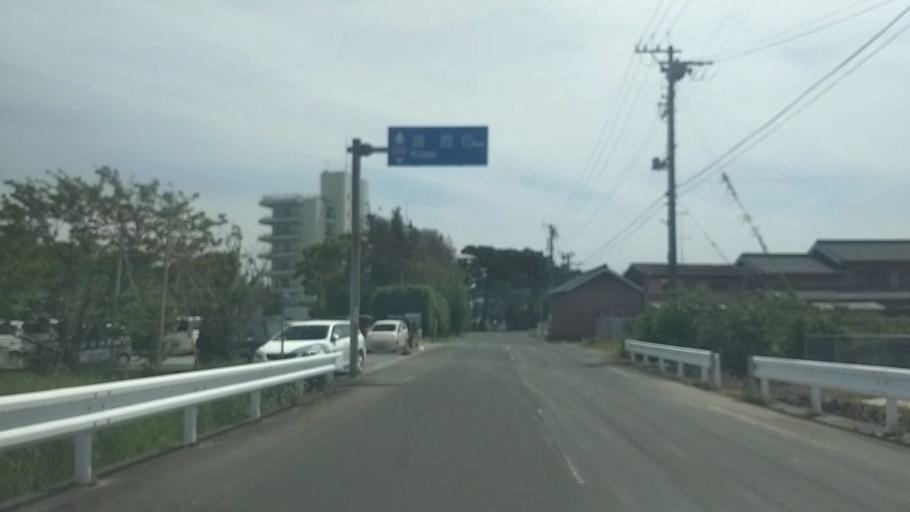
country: JP
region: Shizuoka
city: Kosai-shi
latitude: 34.7880
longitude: 137.5967
